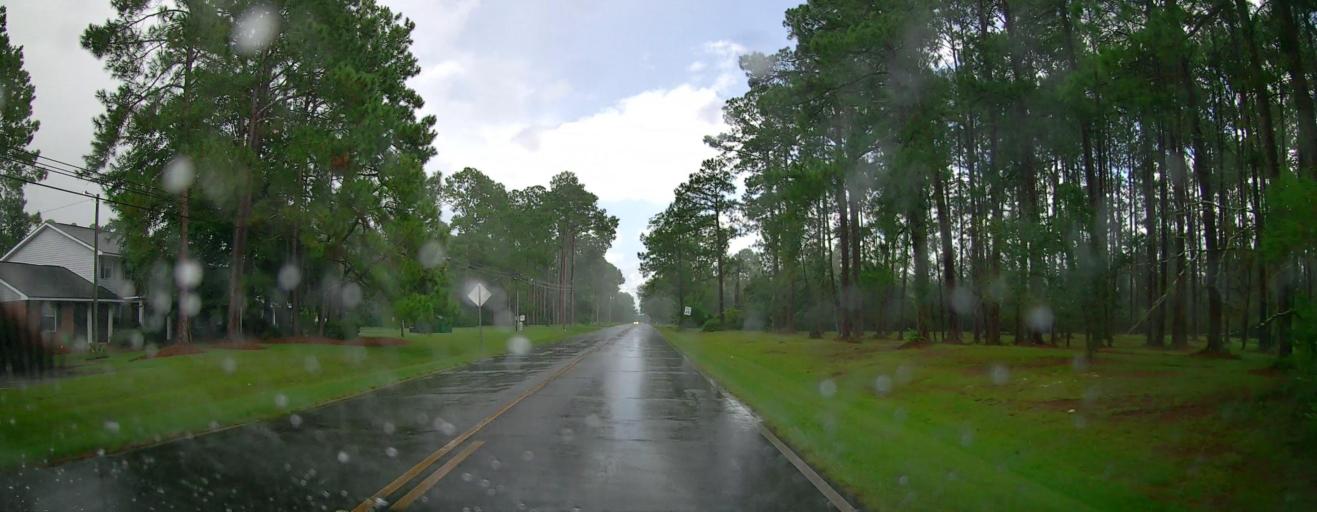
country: US
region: Georgia
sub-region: Ben Hill County
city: Fitzgerald
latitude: 31.7142
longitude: -83.2825
